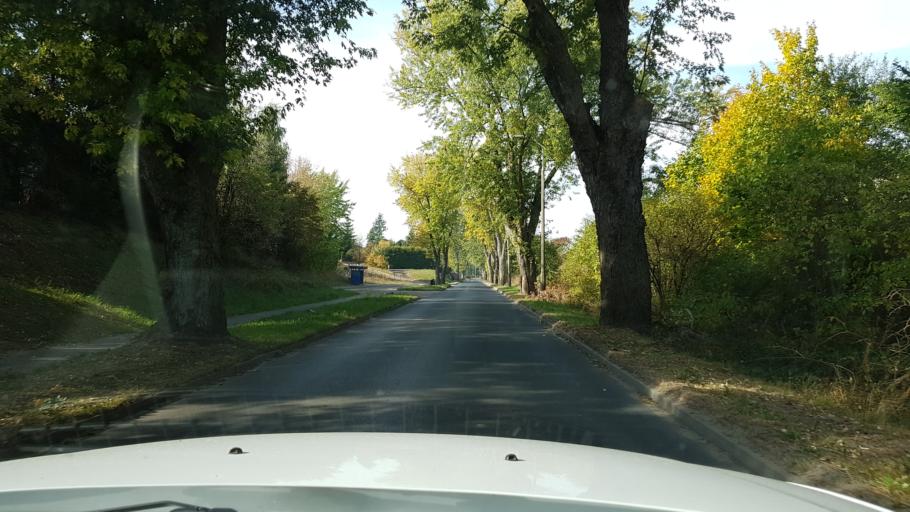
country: PL
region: West Pomeranian Voivodeship
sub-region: Powiat mysliborski
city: Barlinek
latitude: 52.9855
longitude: 15.1937
